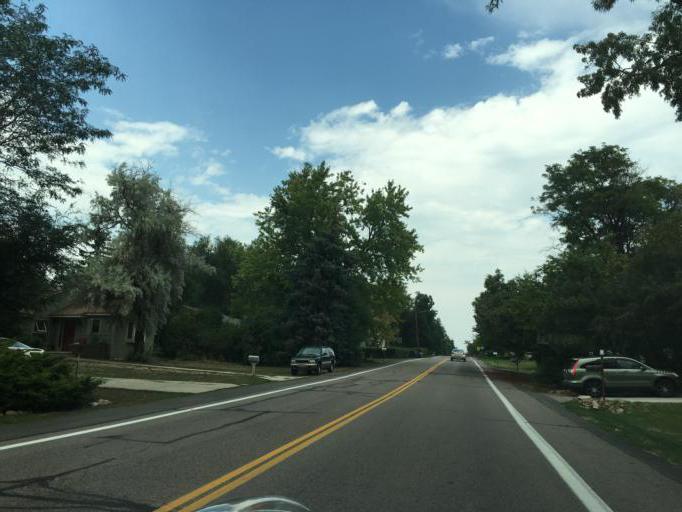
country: US
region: Colorado
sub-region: Jefferson County
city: Wheat Ridge
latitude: 39.7481
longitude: -105.0908
